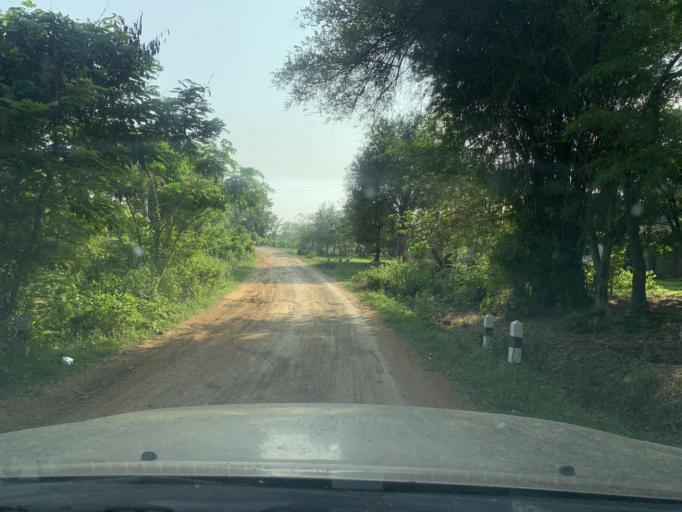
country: TH
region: Uttaradit
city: Ban Khok
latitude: 18.2812
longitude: 101.3136
